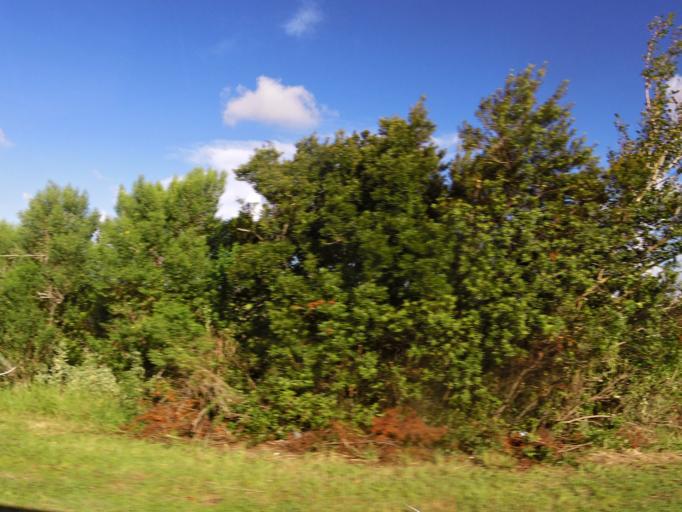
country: US
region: Georgia
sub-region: Glynn County
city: Brunswick
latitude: 31.1277
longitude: -81.4800
